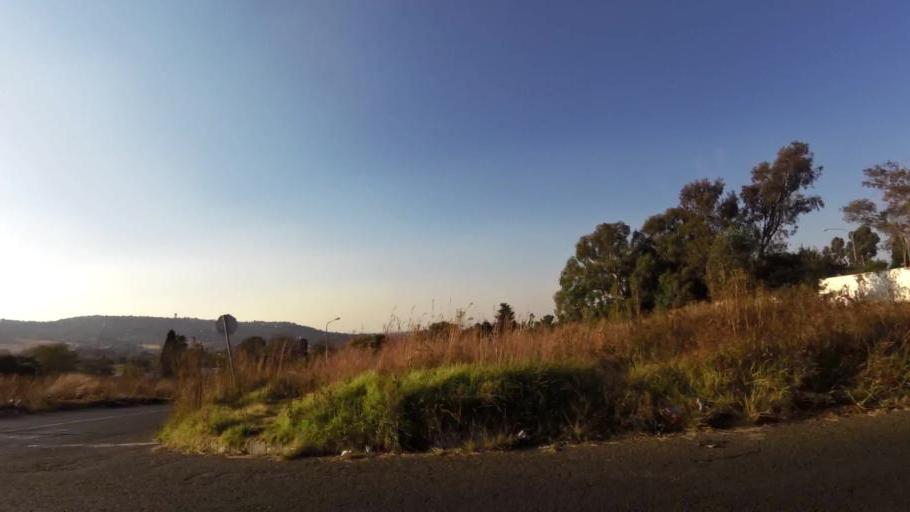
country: ZA
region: Gauteng
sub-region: City of Johannesburg Metropolitan Municipality
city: Johannesburg
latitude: -26.1738
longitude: 27.9729
